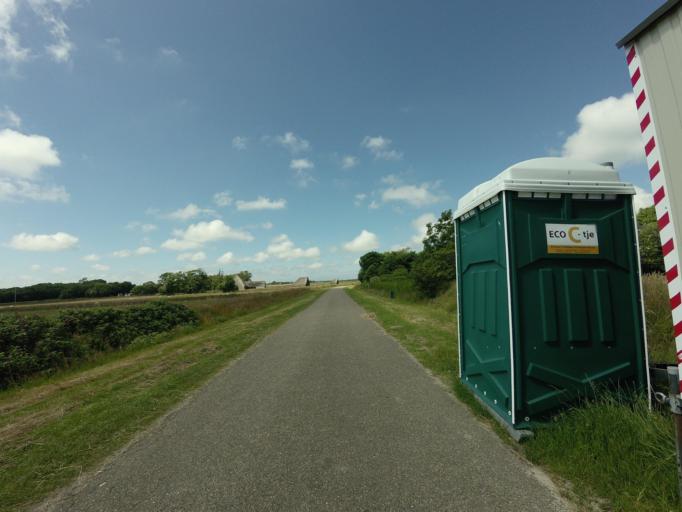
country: NL
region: North Holland
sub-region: Gemeente Texel
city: Den Burg
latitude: 53.0366
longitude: 4.8092
